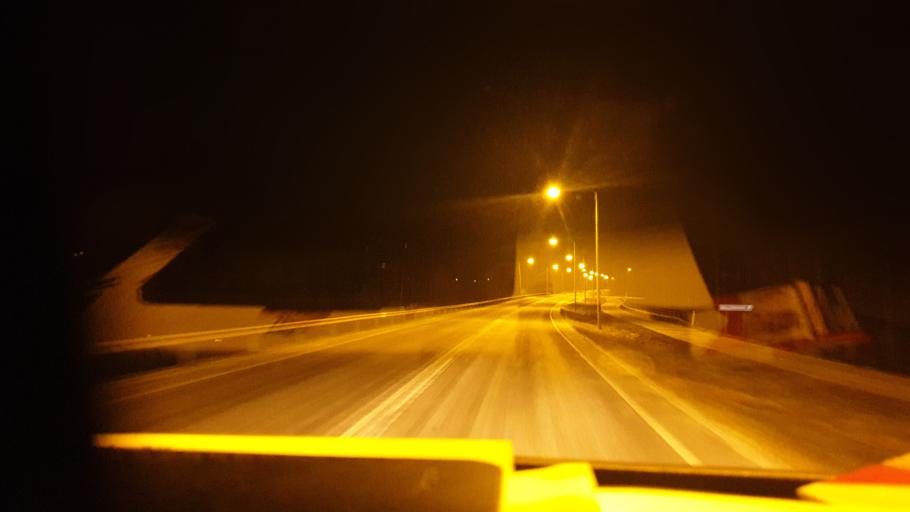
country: FI
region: Southern Ostrobothnia
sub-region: Kuusiokunnat
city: Alavus
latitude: 62.5969
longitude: 23.6576
